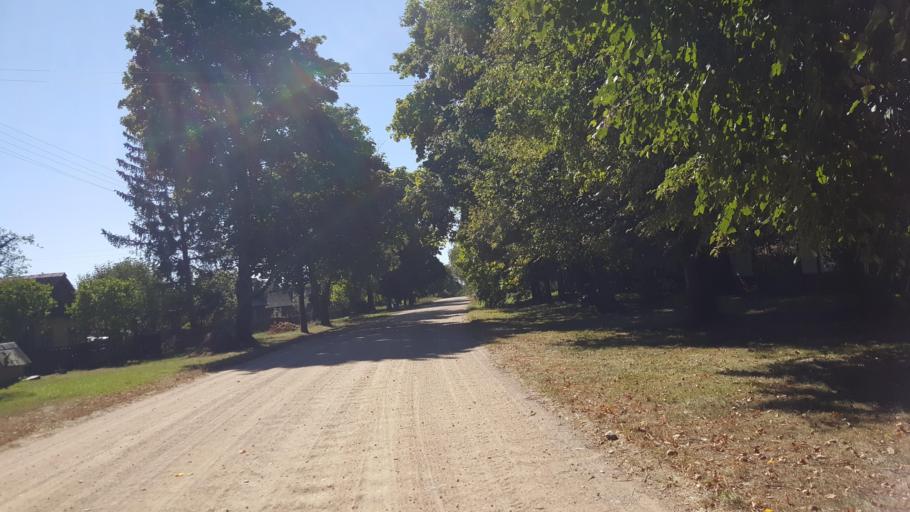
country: PL
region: Lublin Voivodeship
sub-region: Powiat bialski
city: Rokitno
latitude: 52.2150
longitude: 23.3976
